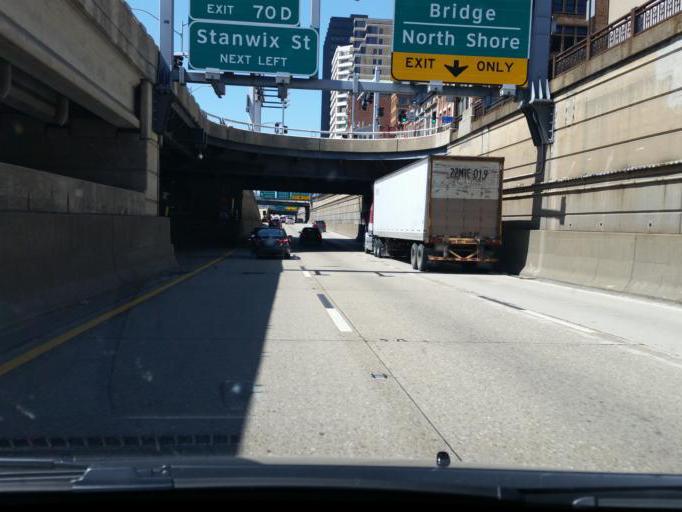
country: US
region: Pennsylvania
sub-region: Allegheny County
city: Pittsburgh
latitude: 40.4371
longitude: -80.0020
